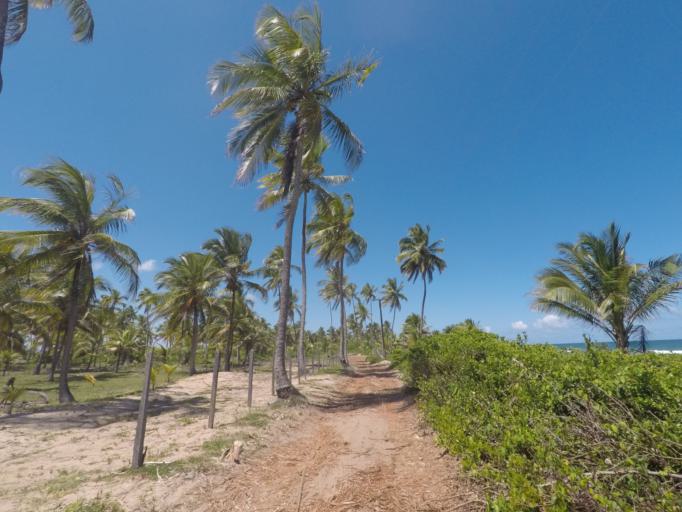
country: BR
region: Bahia
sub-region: Marau
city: Marau
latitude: -14.0027
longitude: -38.9446
